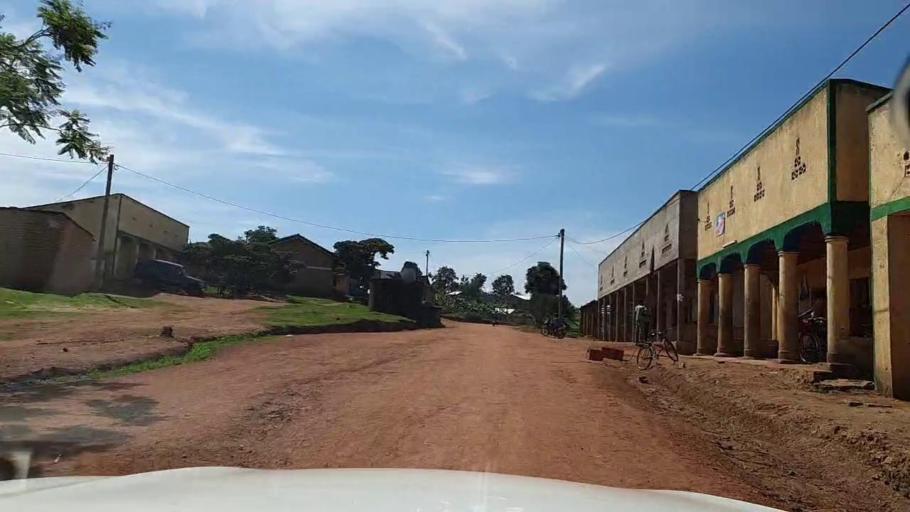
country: RW
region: Southern Province
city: Butare
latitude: -2.6896
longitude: 29.8544
